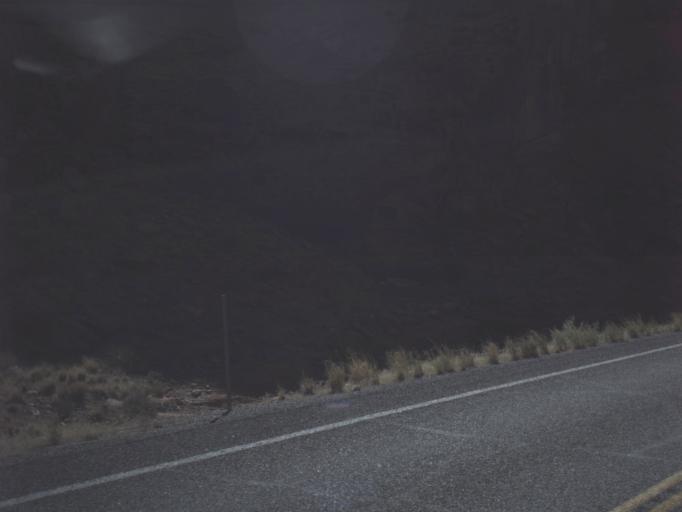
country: US
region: Utah
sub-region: San Juan County
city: Blanding
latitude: 37.9678
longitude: -110.4916
